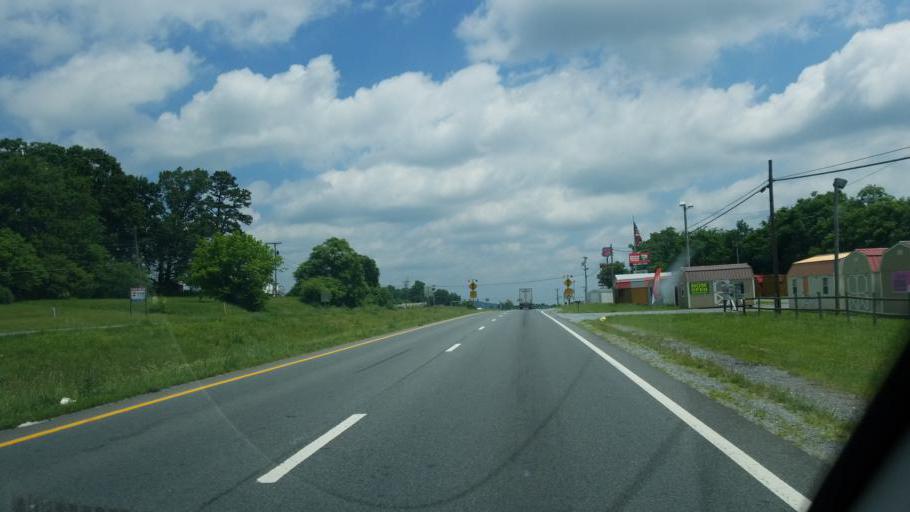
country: US
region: Virginia
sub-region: Campbell County
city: Rustburg
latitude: 37.2778
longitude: -79.1699
